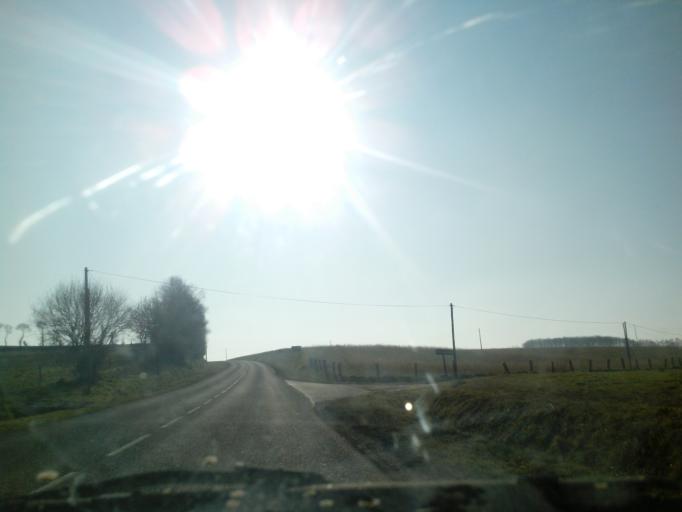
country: FR
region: Brittany
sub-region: Departement des Cotes-d'Armor
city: Merdrignac
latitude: 48.1727
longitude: -2.4336
